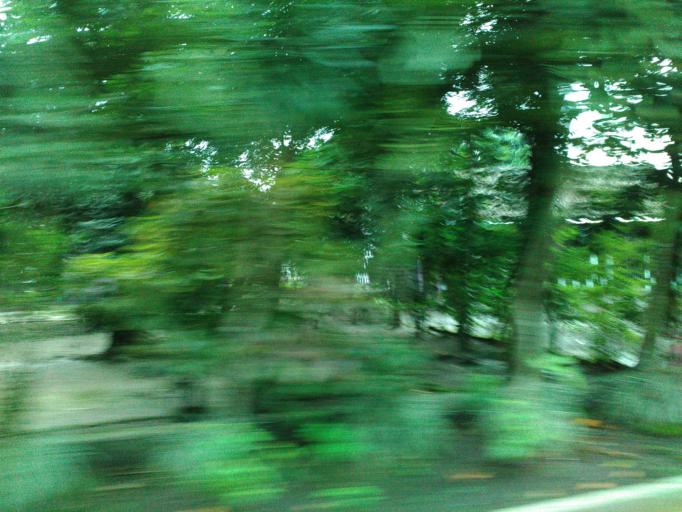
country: ID
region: Central Java
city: Delanggu
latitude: -7.6331
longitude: 110.6976
